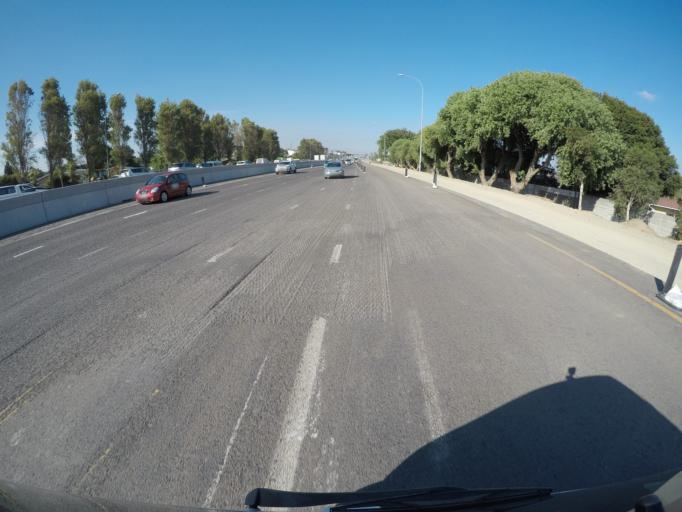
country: ZA
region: Western Cape
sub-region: City of Cape Town
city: Kraaifontein
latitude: -33.8857
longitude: 18.6387
